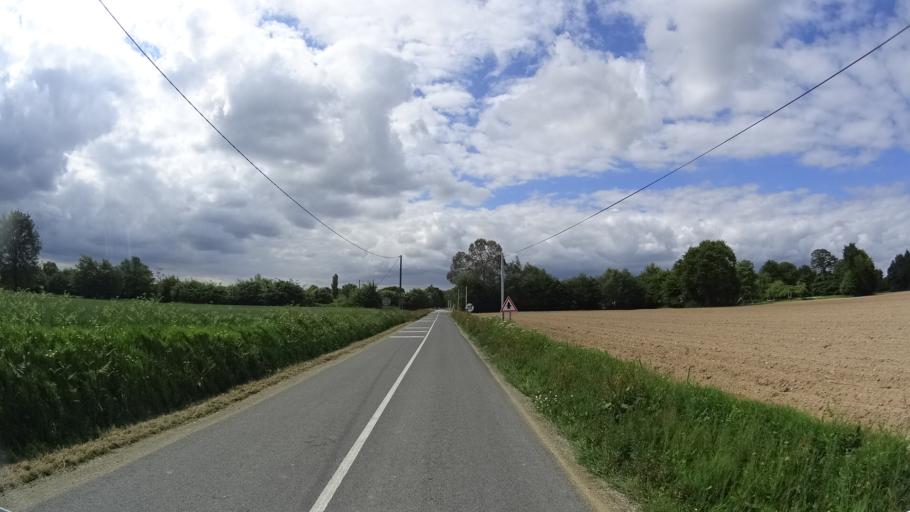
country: FR
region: Brittany
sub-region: Departement d'Ille-et-Vilaine
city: Plelan-le-Grand
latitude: 48.0439
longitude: -2.1006
